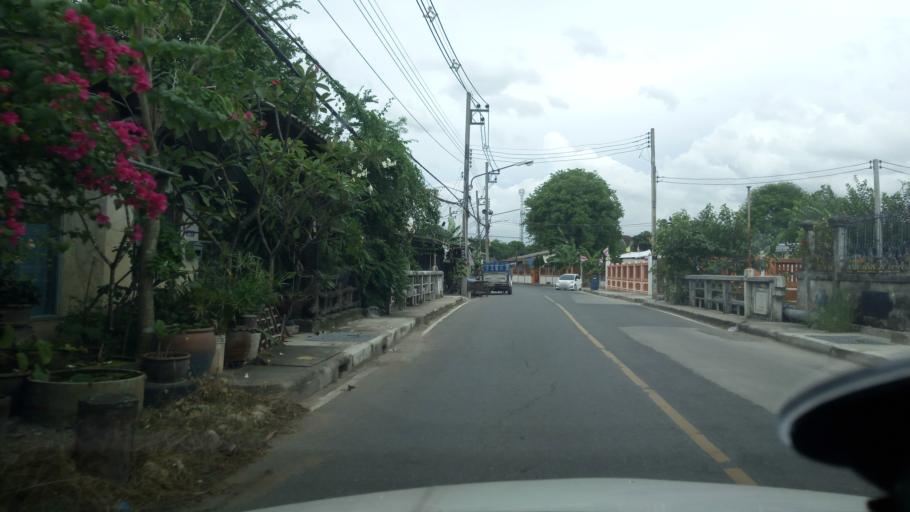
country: TH
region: Chon Buri
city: Phanat Nikhom
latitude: 13.4561
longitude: 101.1778
